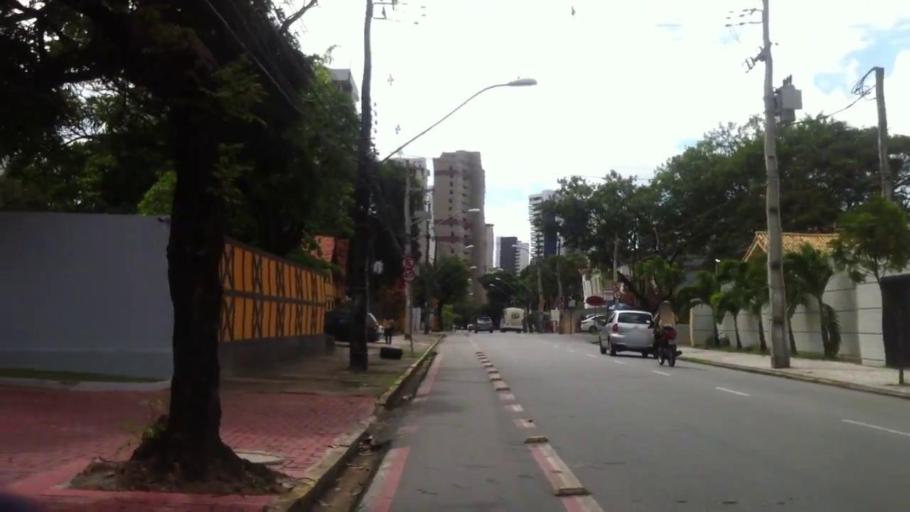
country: BR
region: Pernambuco
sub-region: Recife
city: Recife
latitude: -8.0327
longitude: -34.9116
